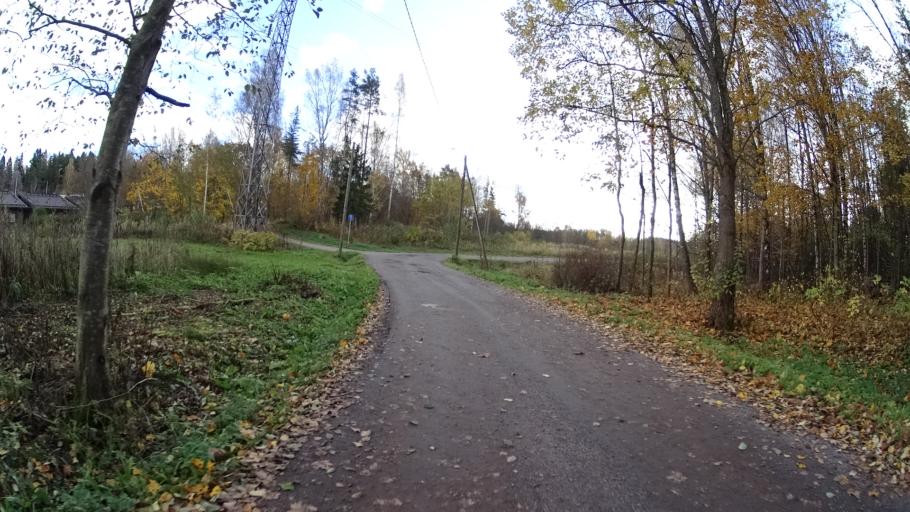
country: FI
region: Uusimaa
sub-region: Helsinki
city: Kilo
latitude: 60.2639
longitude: 24.7939
